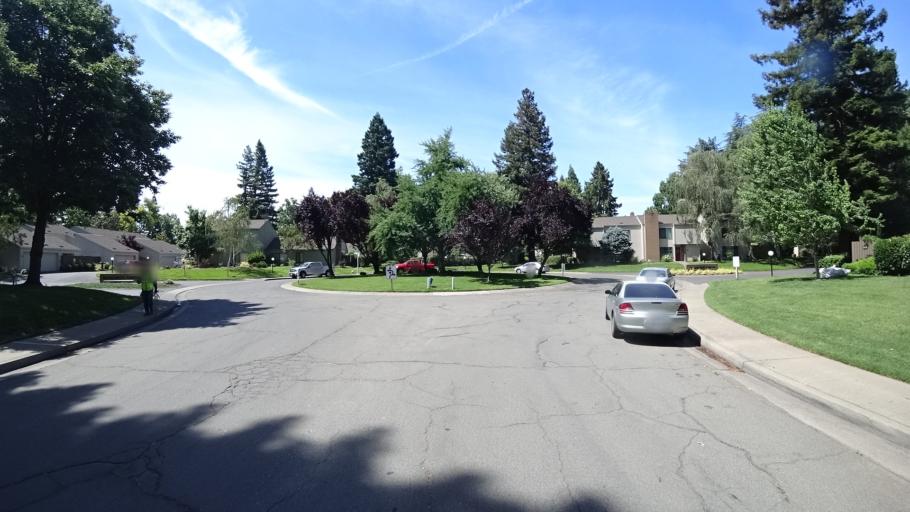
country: US
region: California
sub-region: Sacramento County
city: Rosemont
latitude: 38.5628
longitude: -121.4127
